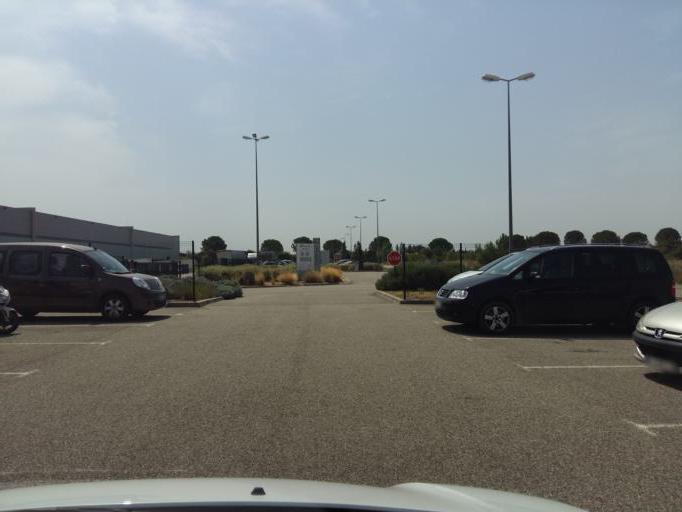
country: FR
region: Provence-Alpes-Cote d'Azur
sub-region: Departement du Vaucluse
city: Lapalud
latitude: 44.2977
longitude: 4.7164
